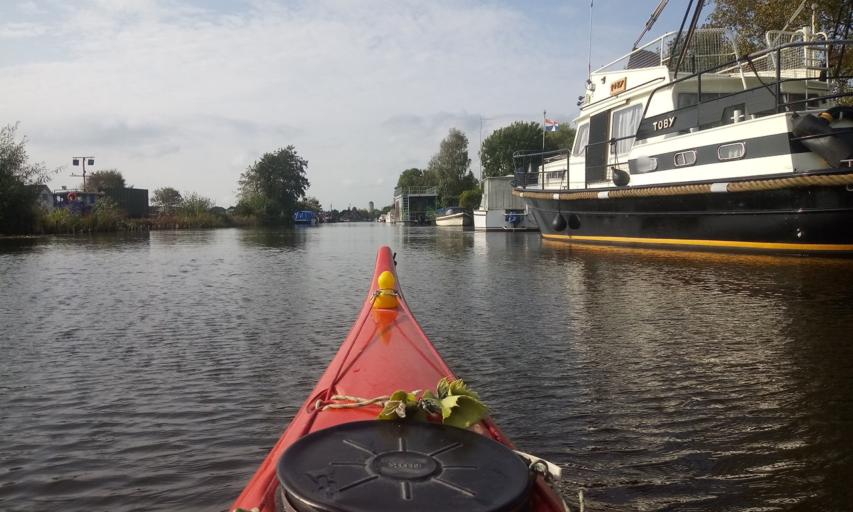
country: NL
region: Utrecht
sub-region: Stichtse Vecht
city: Breukelen
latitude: 52.1840
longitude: 5.0265
